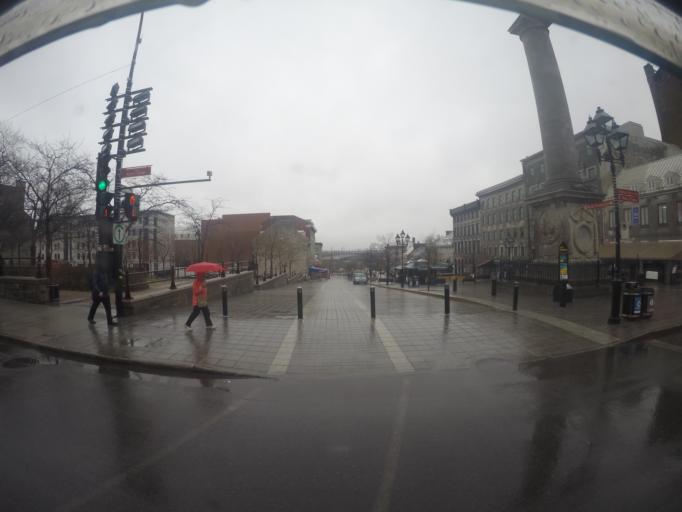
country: CA
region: Quebec
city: Saint-Raymond
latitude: 45.4496
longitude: -73.6209
